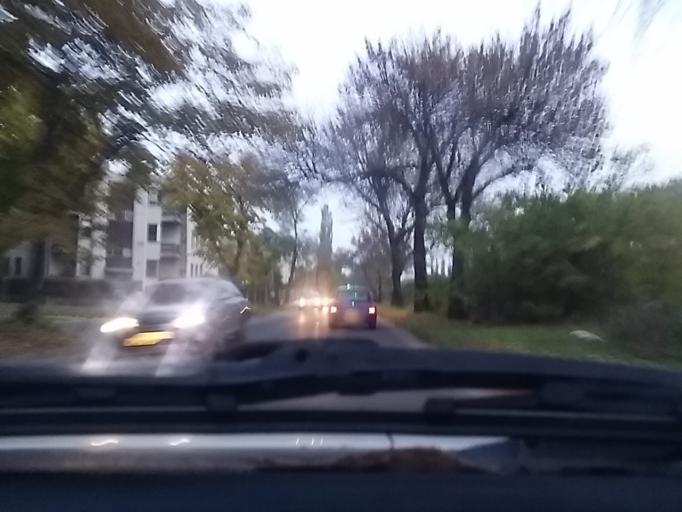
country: HU
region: Budapest
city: Budapest XIV. keruelet
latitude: 47.5238
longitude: 19.1280
